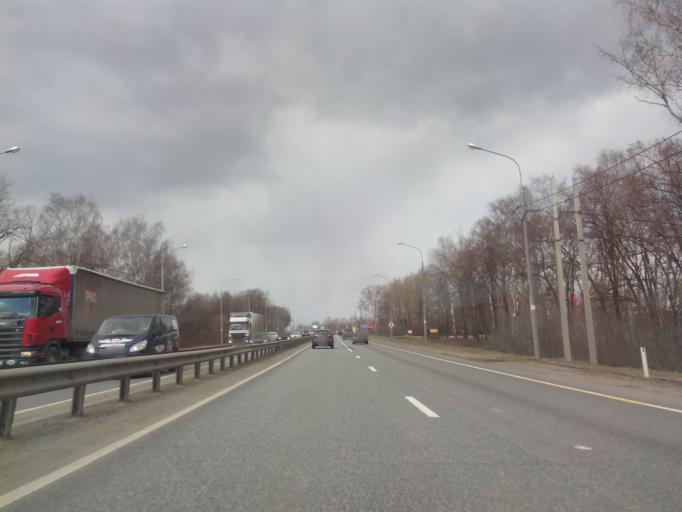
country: RU
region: Moskovskaya
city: Noginsk
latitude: 55.8272
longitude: 38.4159
